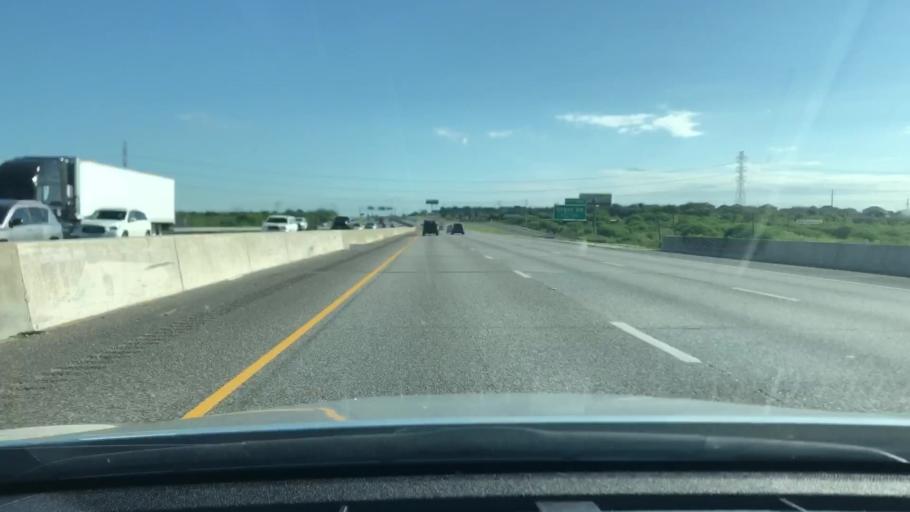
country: US
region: Texas
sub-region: Guadalupe County
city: Northcliff
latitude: 29.6397
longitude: -98.2119
